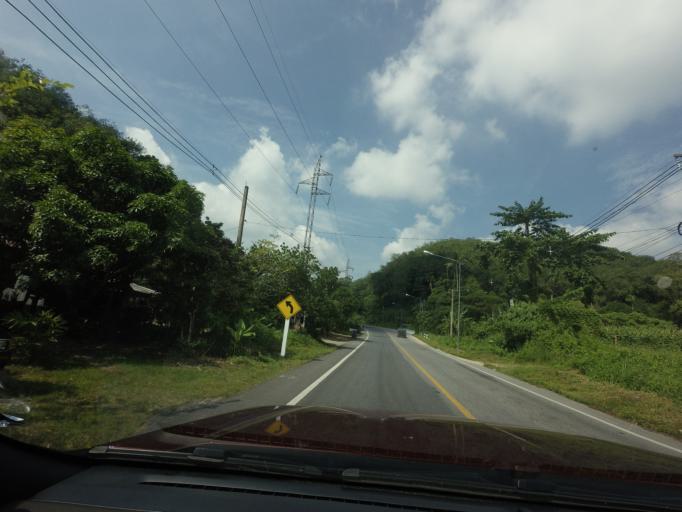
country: TH
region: Yala
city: Betong
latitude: 5.8294
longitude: 101.1124
